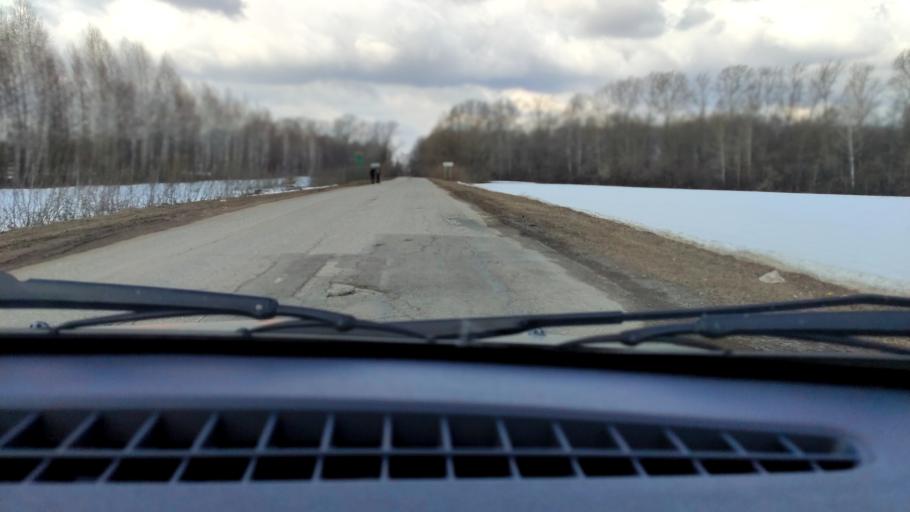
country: RU
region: Bashkortostan
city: Kudeyevskiy
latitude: 54.8641
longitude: 56.7511
